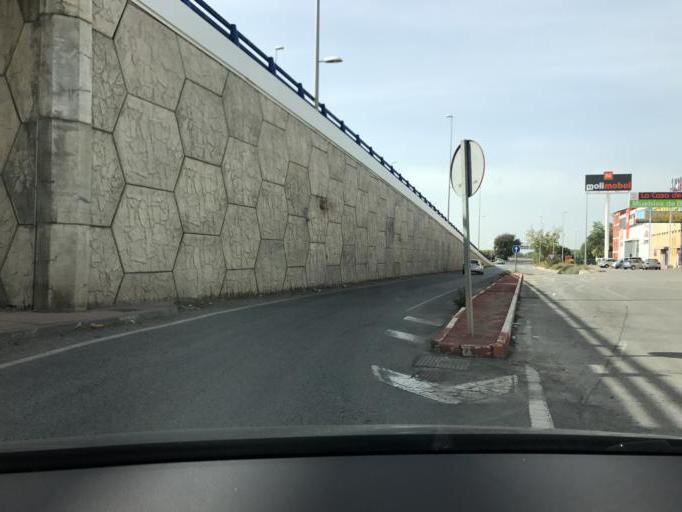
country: ES
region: Andalusia
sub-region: Provincia de Granada
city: Albolote
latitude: 37.2056
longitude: -3.6664
